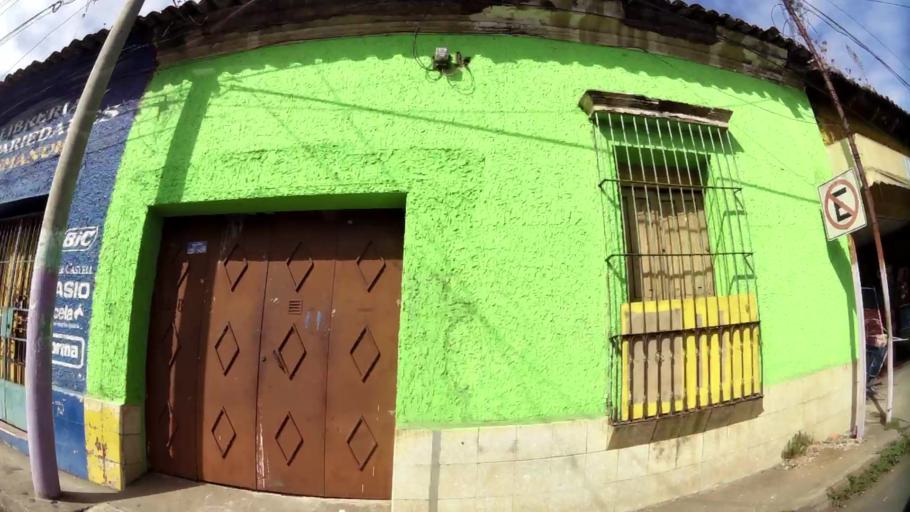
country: SV
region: Santa Ana
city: Chalchuapa
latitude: 13.9864
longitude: -89.6765
